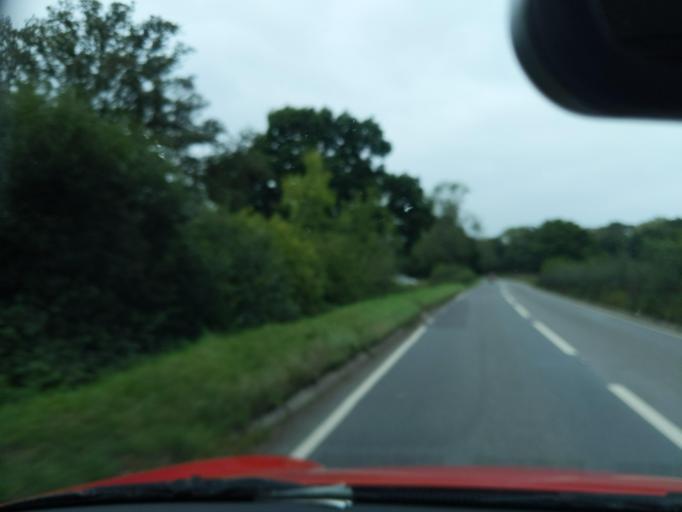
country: GB
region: England
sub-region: Devon
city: Okehampton
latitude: 50.8138
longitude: -4.0692
